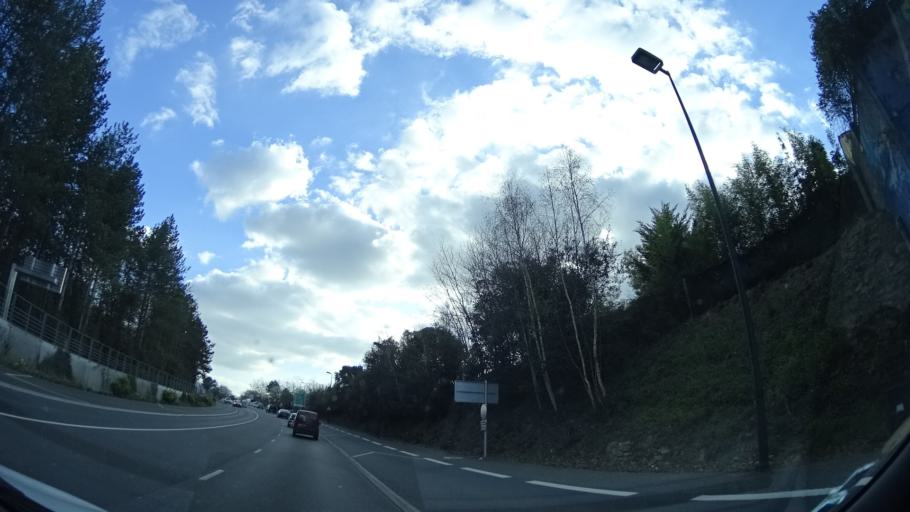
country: FR
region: Pays de la Loire
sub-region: Departement de la Loire-Atlantique
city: Sainte-Luce-sur-Loire
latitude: 47.2571
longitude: -1.5292
